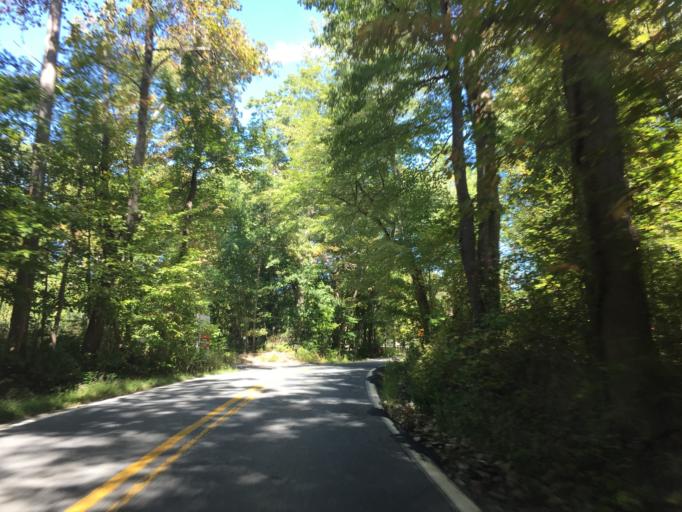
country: US
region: Maryland
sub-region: Baltimore County
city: White Marsh
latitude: 39.3929
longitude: -76.4155
